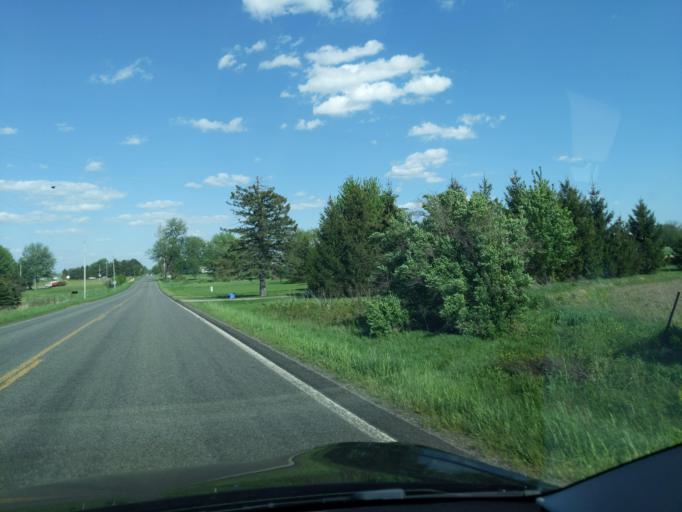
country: US
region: Michigan
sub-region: Ionia County
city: Lake Odessa
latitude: 42.7843
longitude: -85.1882
